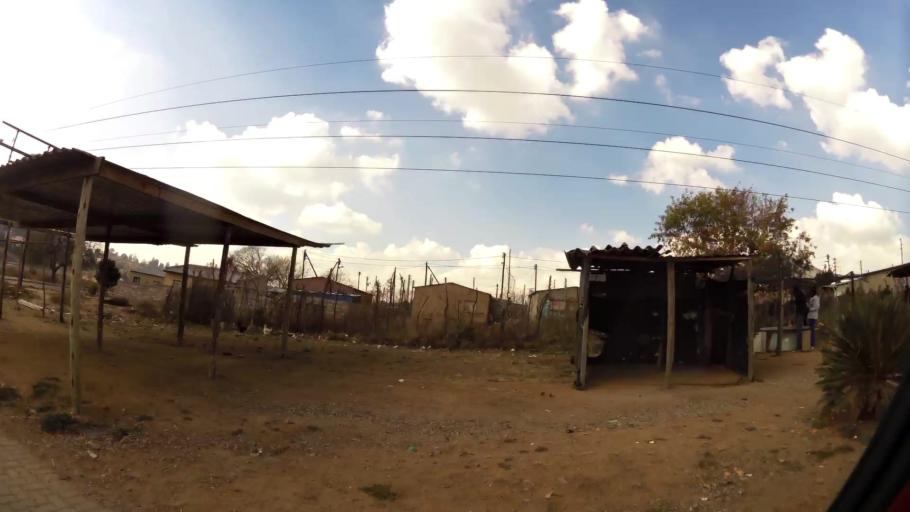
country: ZA
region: Gauteng
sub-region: City of Johannesburg Metropolitan Municipality
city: Roodepoort
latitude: -26.1822
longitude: 27.8516
